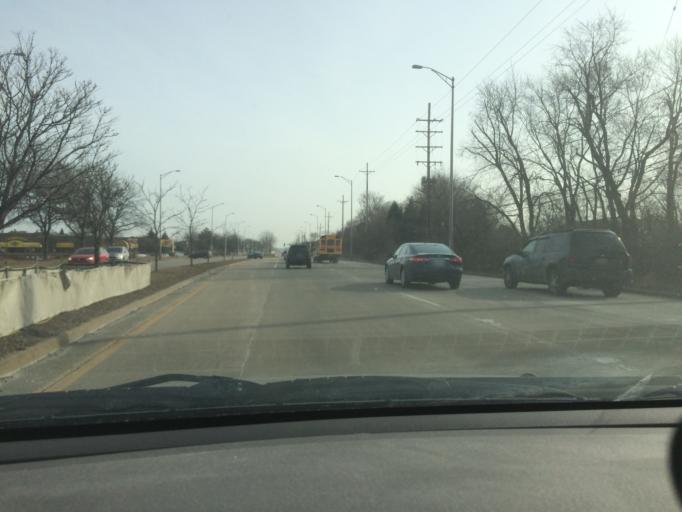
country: US
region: Illinois
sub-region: Cook County
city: Hoffman Estates
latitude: 42.0497
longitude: -88.0701
